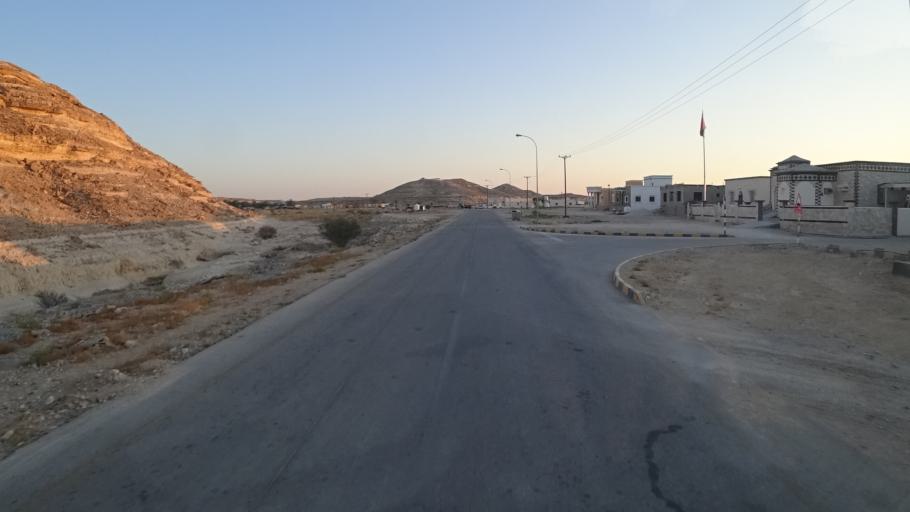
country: OM
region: Zufar
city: Salalah
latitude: 17.4851
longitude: 53.3491
